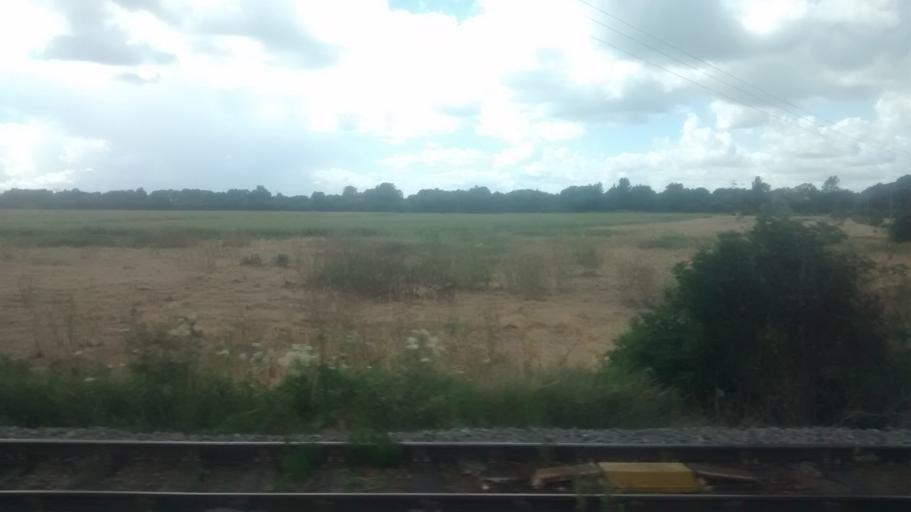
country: GB
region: England
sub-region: Cambridgeshire
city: Ely
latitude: 52.3835
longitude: 0.2606
